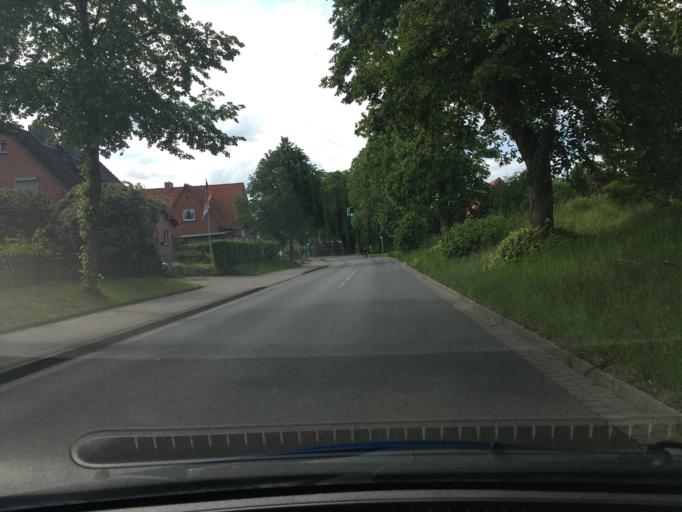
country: DE
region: Lower Saxony
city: Handeloh
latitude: 53.2450
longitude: 9.8411
